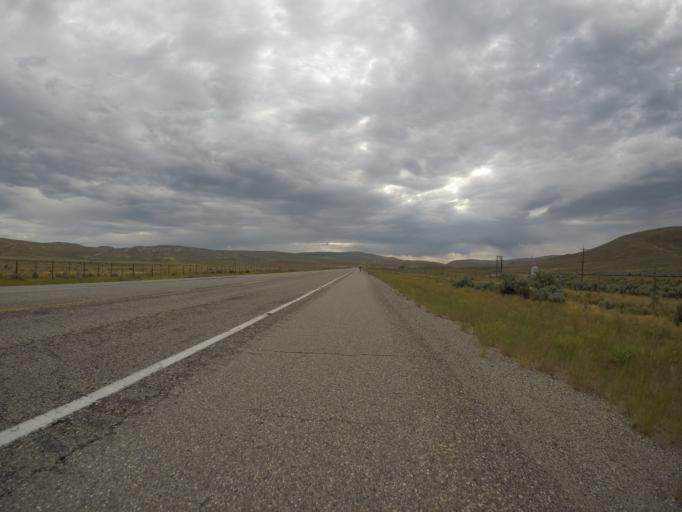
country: US
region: Utah
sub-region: Rich County
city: Randolph
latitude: 41.8239
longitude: -110.9286
